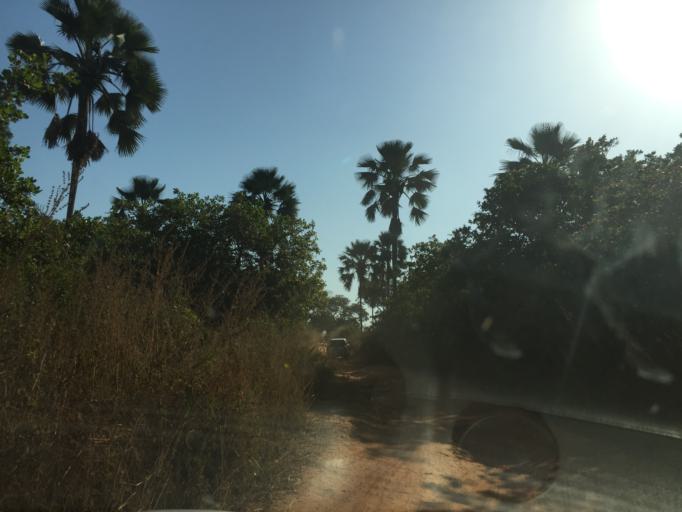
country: GW
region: Oio
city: Farim
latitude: 12.4585
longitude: -15.3060
